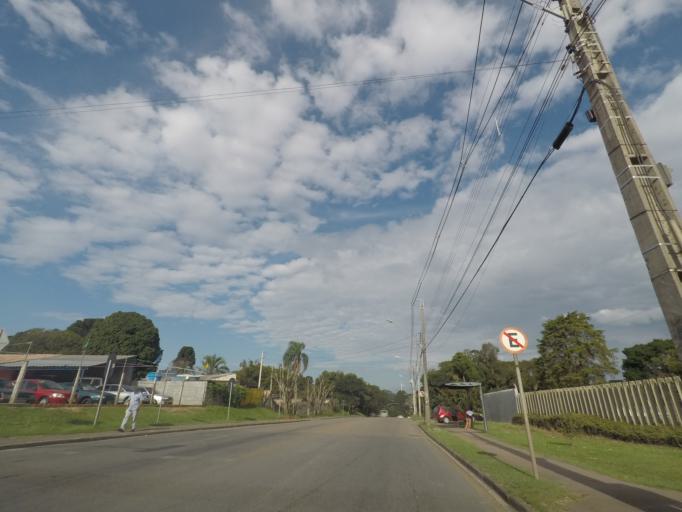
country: BR
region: Parana
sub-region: Sao Jose Dos Pinhais
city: Sao Jose dos Pinhais
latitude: -25.5685
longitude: -49.2837
